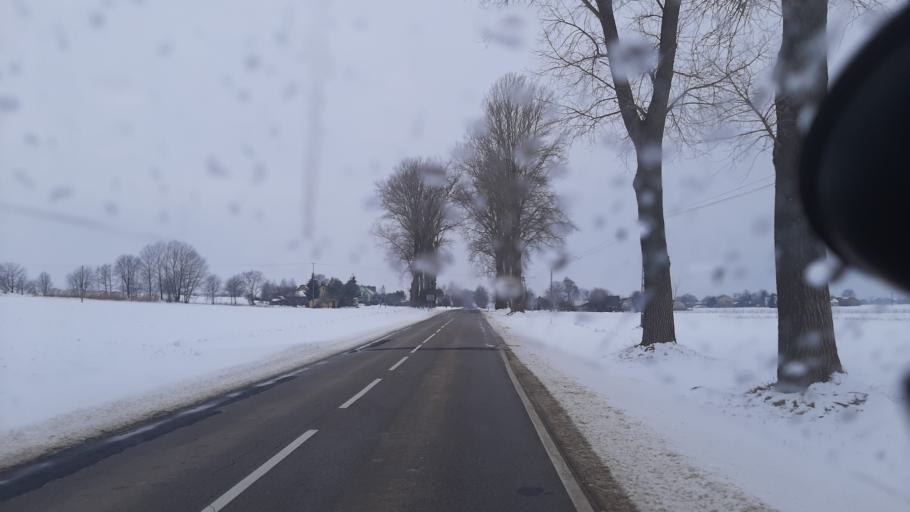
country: PL
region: Lublin Voivodeship
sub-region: Powiat lubelski
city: Jastkow
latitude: 51.3450
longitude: 22.3926
